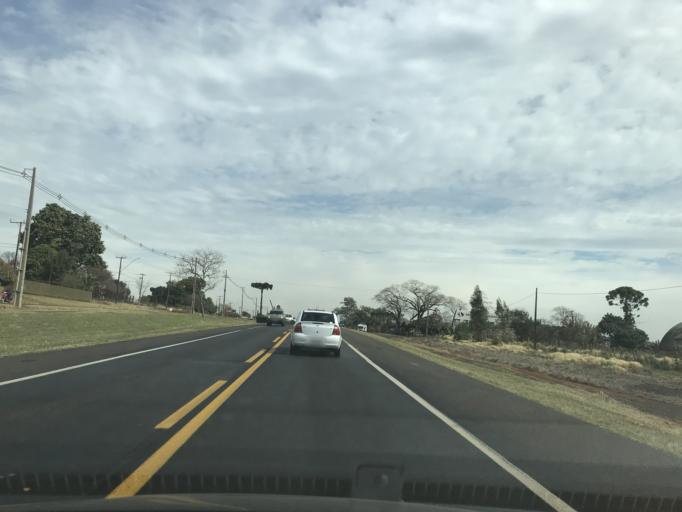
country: BR
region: Parana
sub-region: Cascavel
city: Cascavel
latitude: -25.0424
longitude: -53.6039
